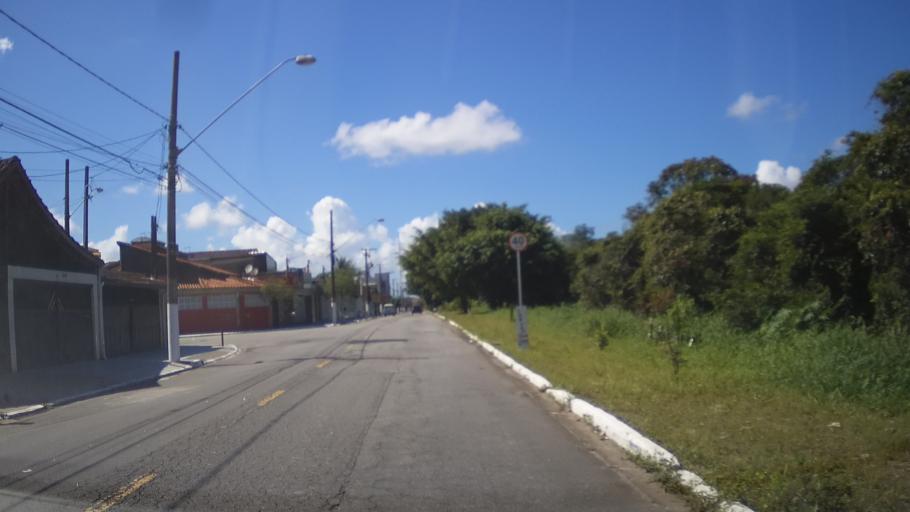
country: BR
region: Sao Paulo
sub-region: Praia Grande
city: Praia Grande
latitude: -24.0310
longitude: -46.5006
